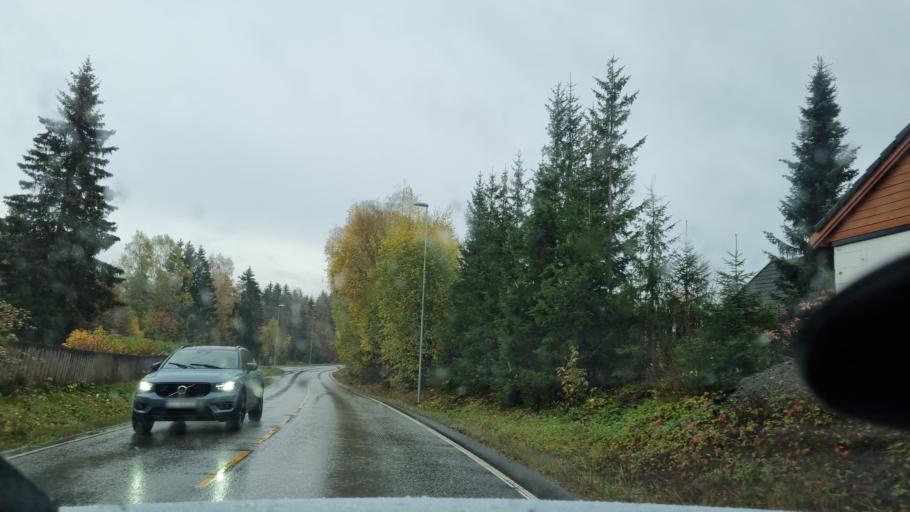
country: NO
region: Hedmark
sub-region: Hamar
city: Hamar
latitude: 60.8208
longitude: 11.0601
